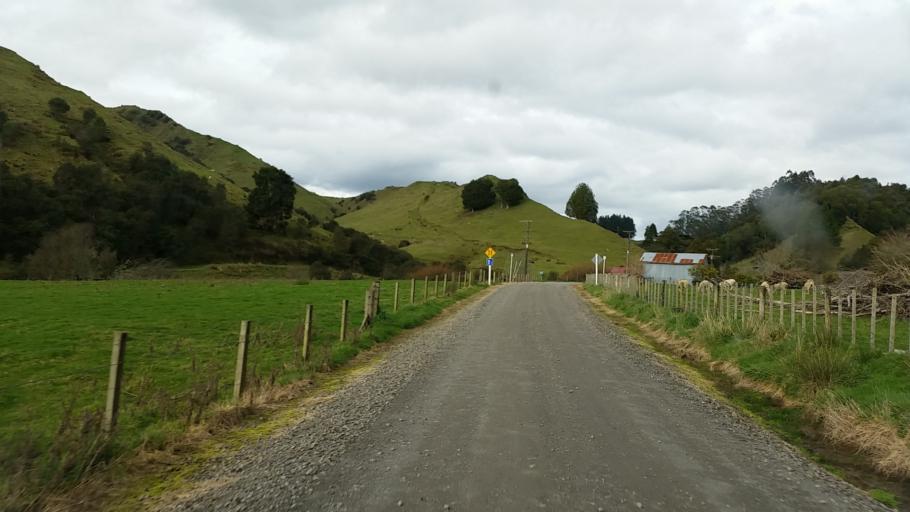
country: NZ
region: Taranaki
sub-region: New Plymouth District
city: Waitara
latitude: -39.1579
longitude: 174.5618
